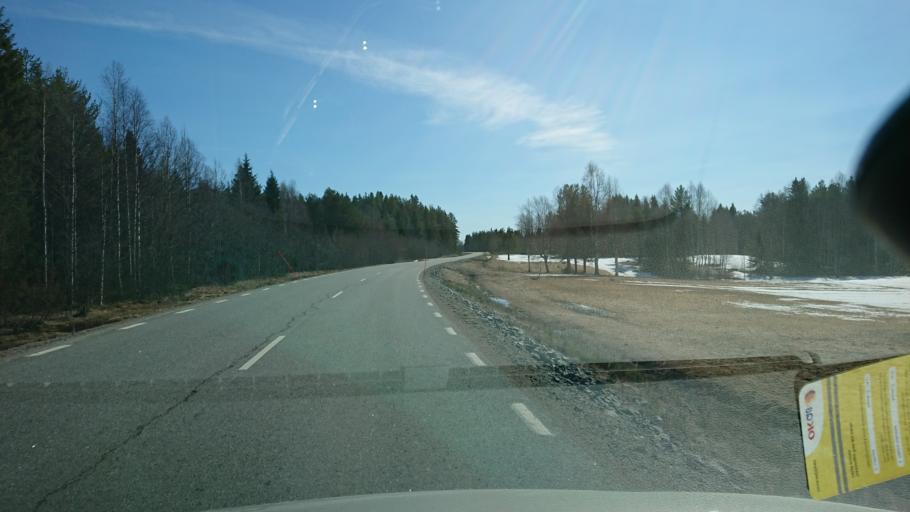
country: SE
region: Vaesternorrland
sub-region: Solleftea Kommun
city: As
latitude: 63.6642
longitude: 16.4426
